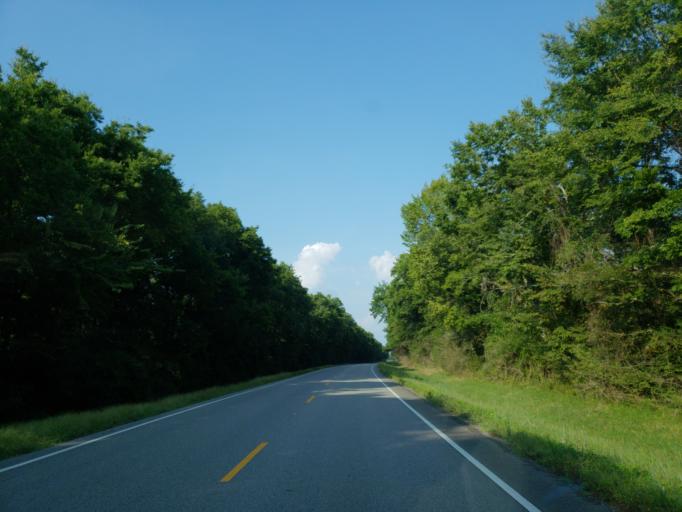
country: US
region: Alabama
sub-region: Greene County
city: Eutaw
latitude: 32.7463
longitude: -88.0450
